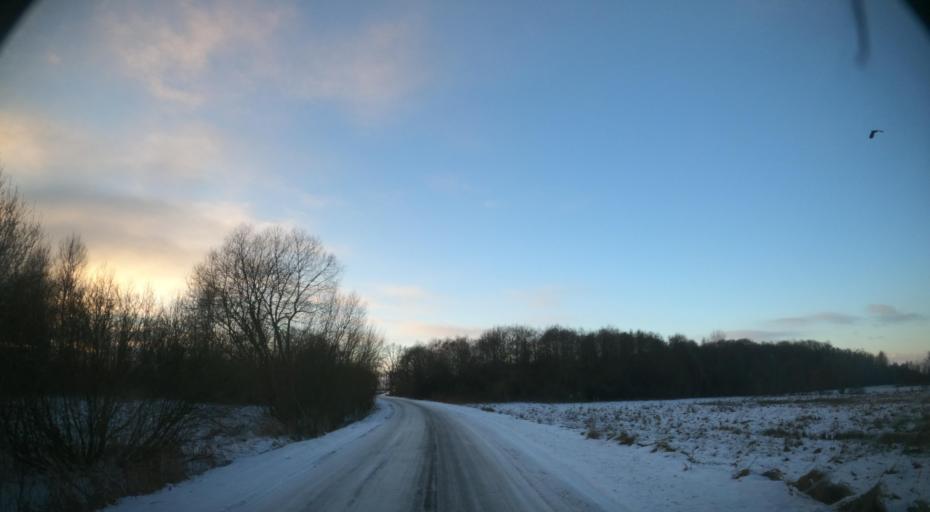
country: PL
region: West Pomeranian Voivodeship
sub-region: Powiat slawienski
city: Darlowo
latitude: 54.2992
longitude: 16.3996
